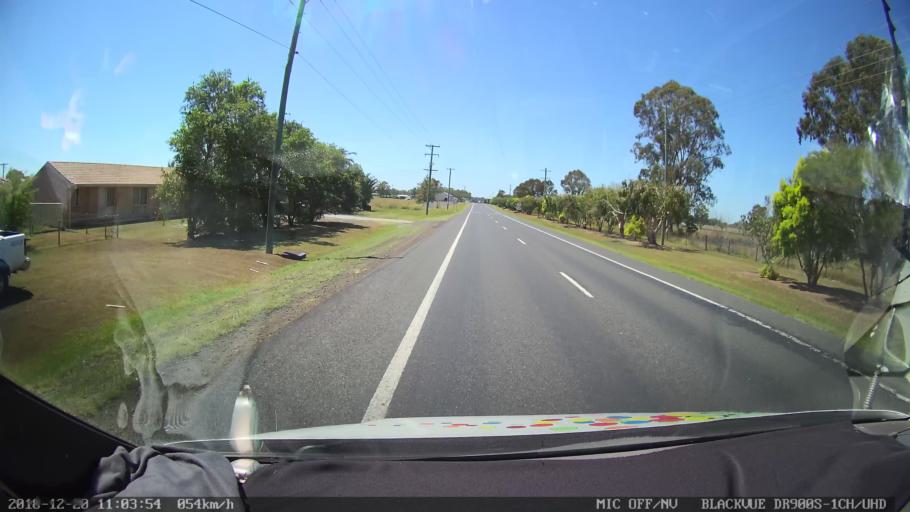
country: AU
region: New South Wales
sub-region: Richmond Valley
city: Casino
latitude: -28.8805
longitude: 153.0430
